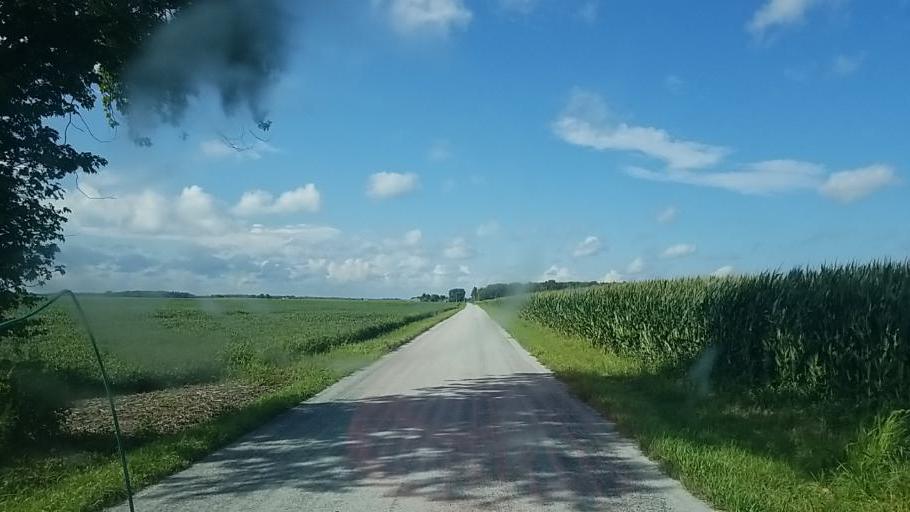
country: US
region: Ohio
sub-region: Hardin County
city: Kenton
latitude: 40.6832
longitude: -83.5310
